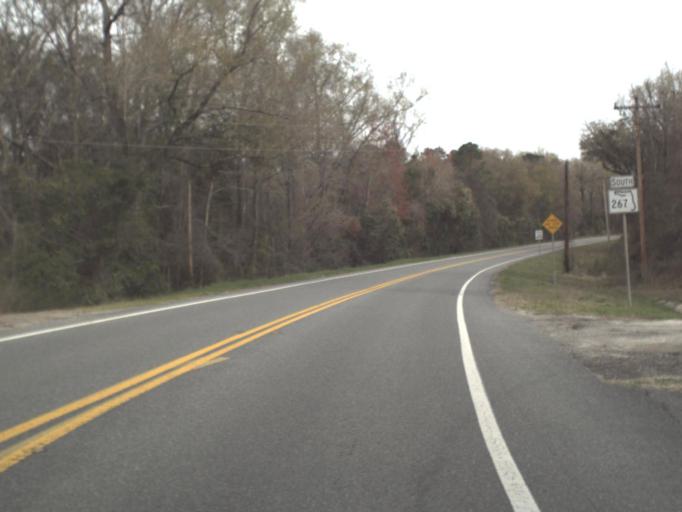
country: US
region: Florida
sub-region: Wakulla County
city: Crawfordville
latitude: 30.2524
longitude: -84.3231
